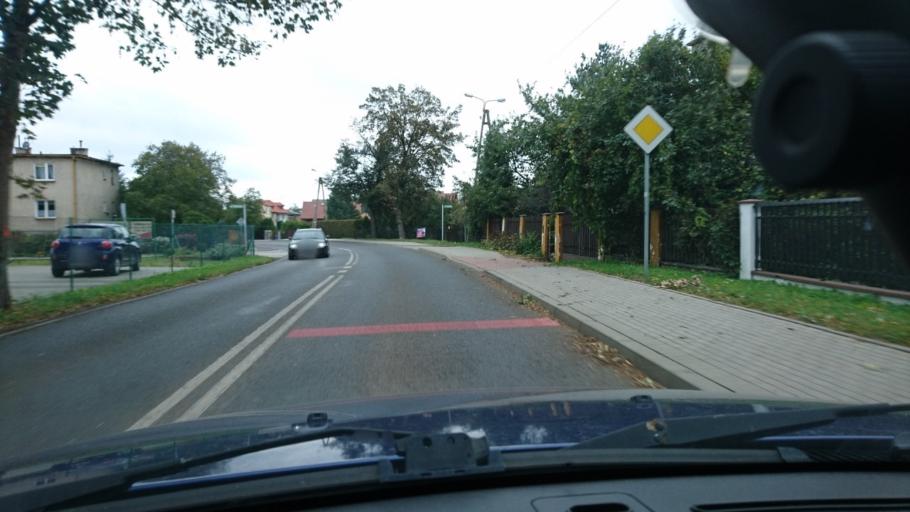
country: PL
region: Silesian Voivodeship
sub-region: Powiat bielski
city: Jaworze
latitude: 49.8026
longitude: 18.9831
